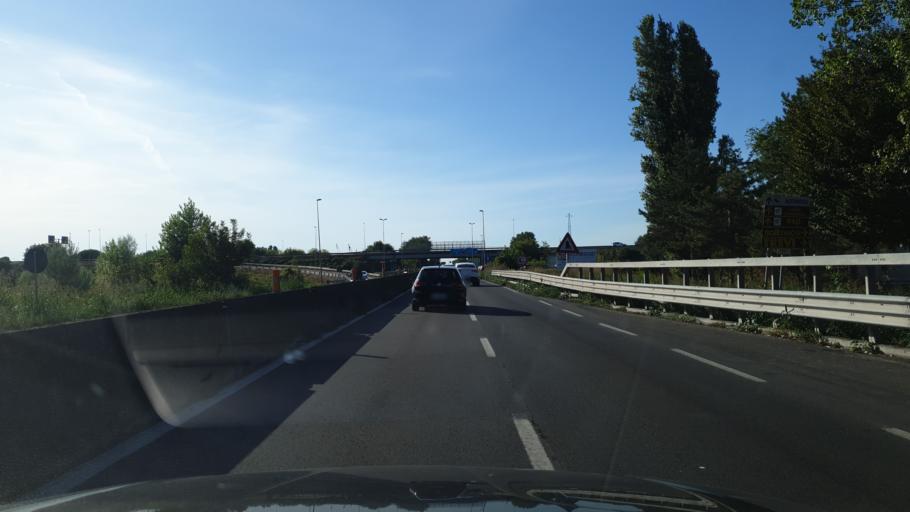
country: IT
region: Emilia-Romagna
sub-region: Provincia di Ravenna
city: Madonna Dell'Albero
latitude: 44.3790
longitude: 12.2117
